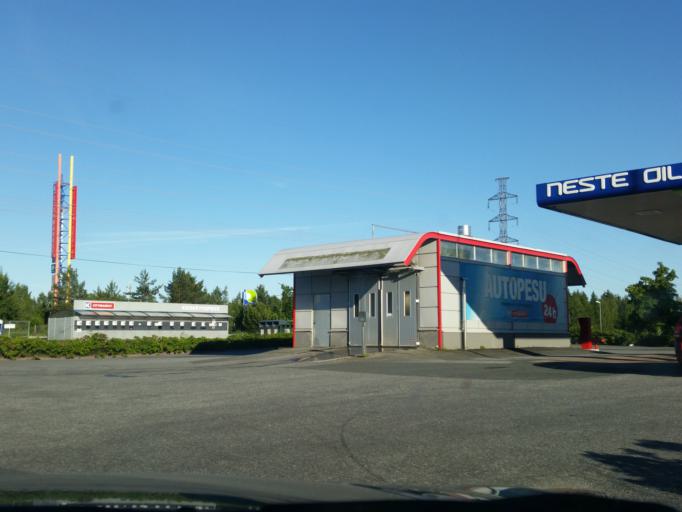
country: FI
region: Northern Savo
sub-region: Kuopio
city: Kuopio
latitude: 62.8630
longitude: 27.6147
